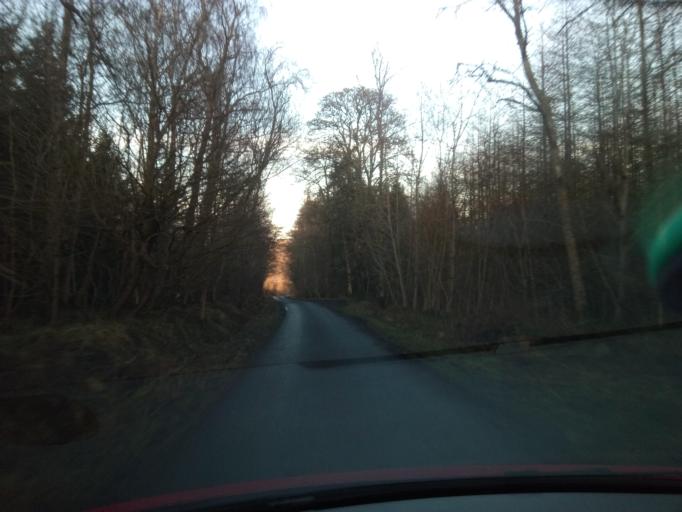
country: GB
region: Scotland
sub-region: The Scottish Borders
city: Melrose
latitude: 55.5864
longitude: -2.7396
